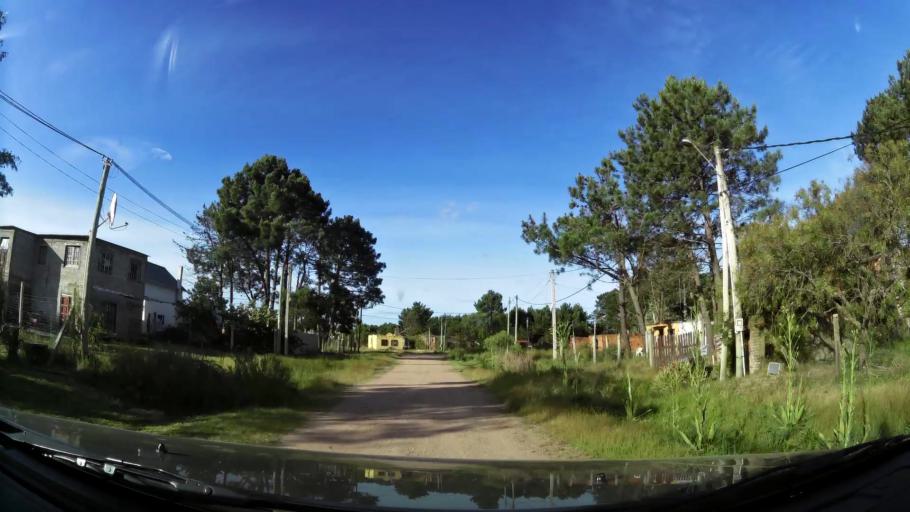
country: UY
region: Canelones
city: Empalme Olmos
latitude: -34.7689
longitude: -55.8573
